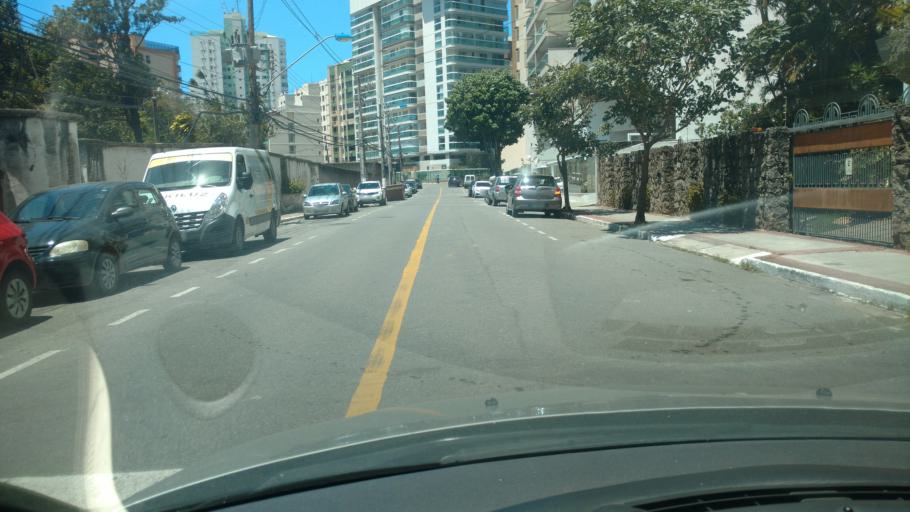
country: BR
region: Espirito Santo
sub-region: Vila Velha
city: Vila Velha
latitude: -20.3303
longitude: -40.2779
